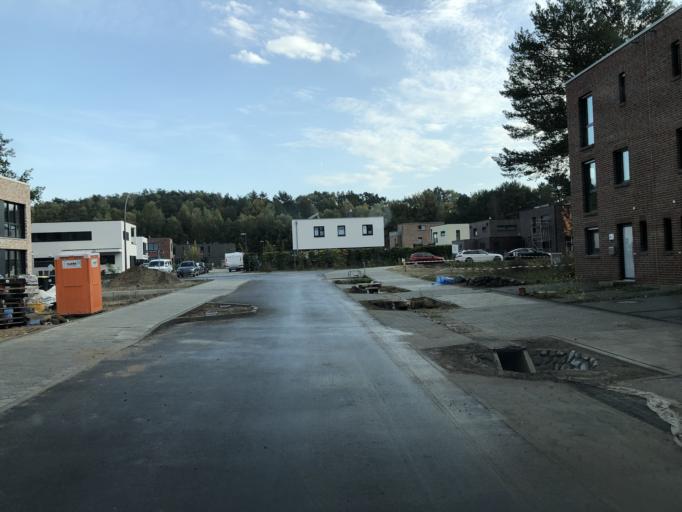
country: DE
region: Lower Saxony
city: Neu Wulmstorf
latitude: 53.4650
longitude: 9.8159
